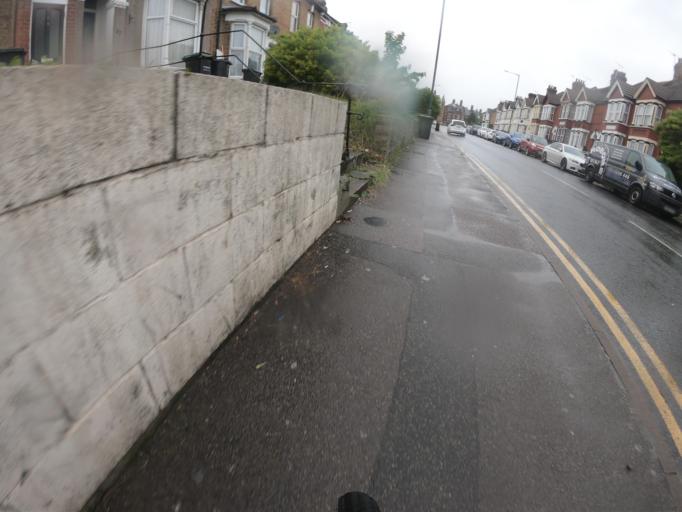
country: GB
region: England
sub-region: Kent
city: Gravesend
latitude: 51.4365
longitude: 0.3569
